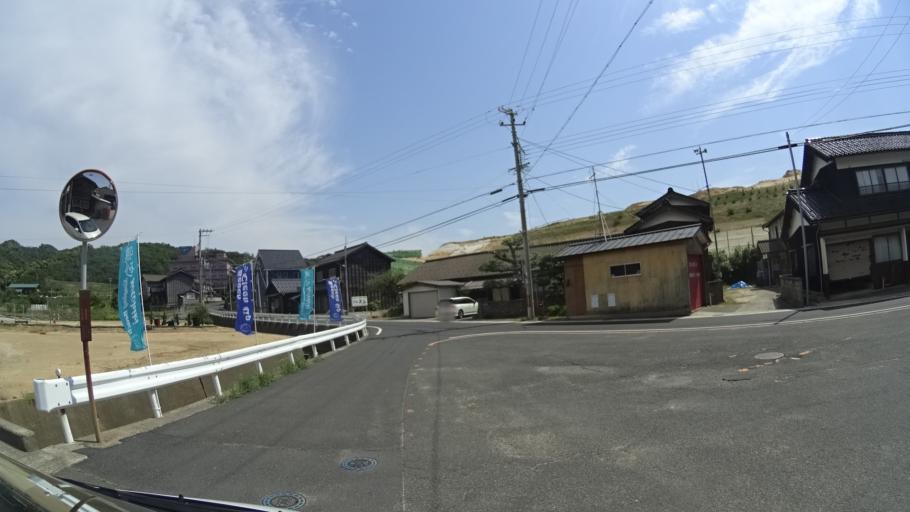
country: JP
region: Kyoto
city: Miyazu
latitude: 35.6996
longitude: 135.0542
